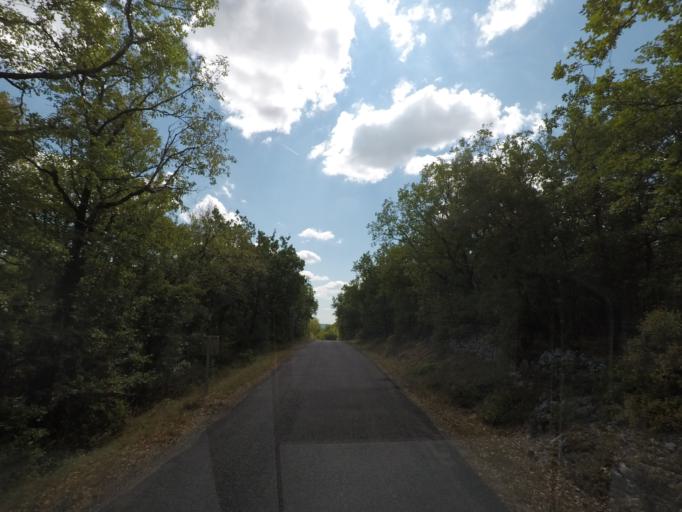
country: FR
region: Midi-Pyrenees
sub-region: Departement du Lot
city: Cajarc
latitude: 44.5331
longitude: 1.6632
